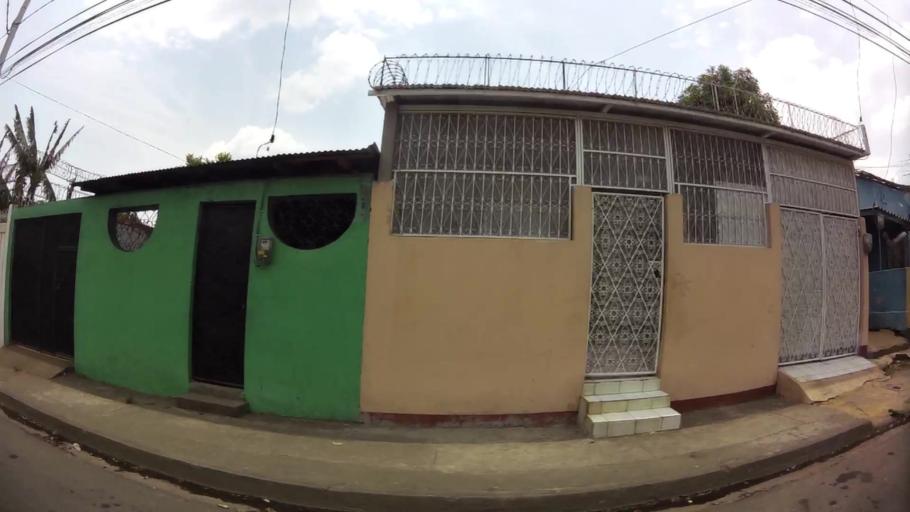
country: NI
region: Managua
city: Managua
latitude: 12.1185
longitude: -86.2973
